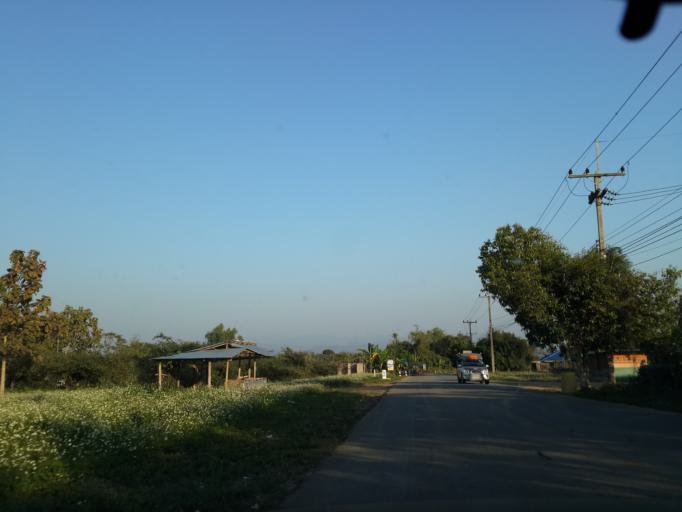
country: TH
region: Chiang Mai
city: Chai Prakan
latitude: 19.8129
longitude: 99.1151
